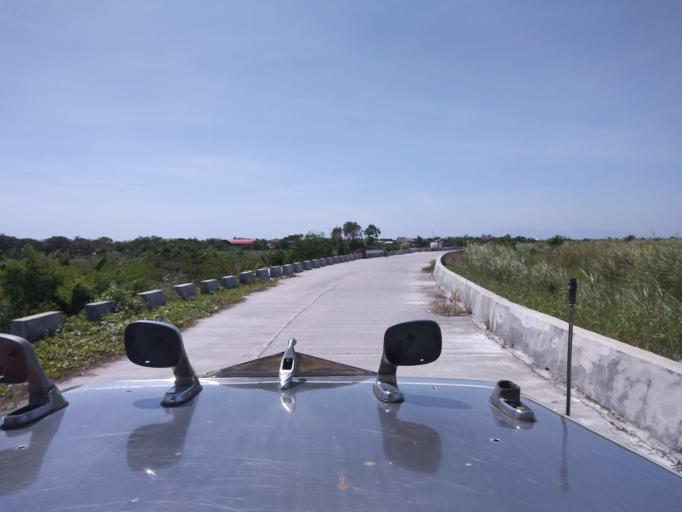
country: PH
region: Central Luzon
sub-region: Province of Pampanga
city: Minalin
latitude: 14.9860
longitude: 120.6942
